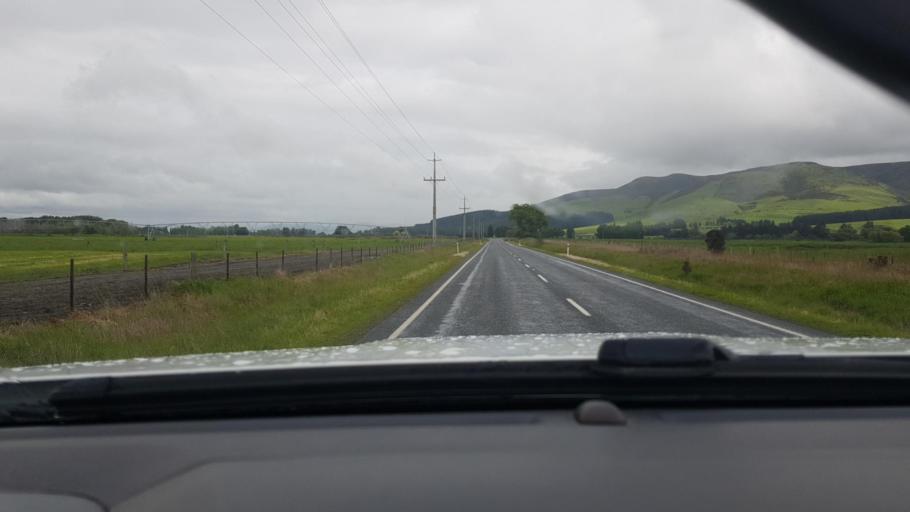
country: NZ
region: Southland
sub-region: Southland District
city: Winton
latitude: -45.7931
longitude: 168.3837
